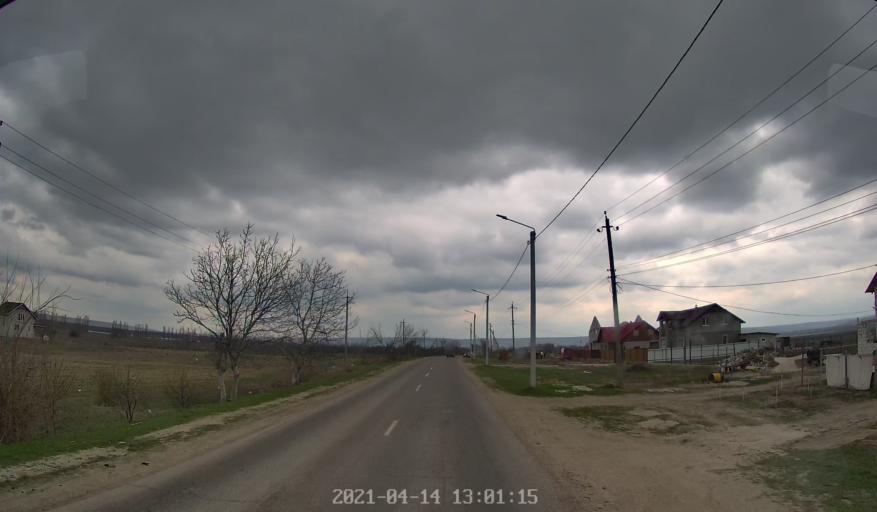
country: MD
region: Chisinau
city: Vadul lui Voda
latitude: 47.1332
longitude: 29.1175
